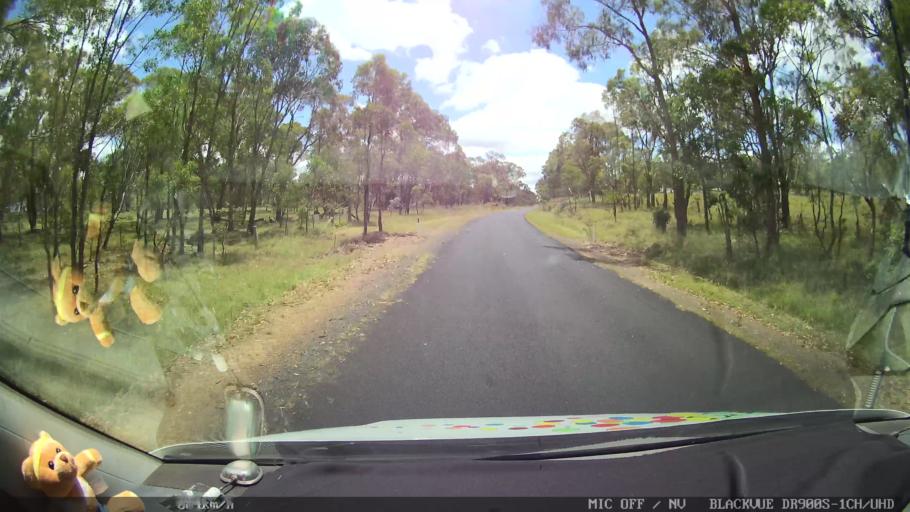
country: AU
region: New South Wales
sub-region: Glen Innes Severn
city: Glen Innes
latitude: -29.4325
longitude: 151.6857
